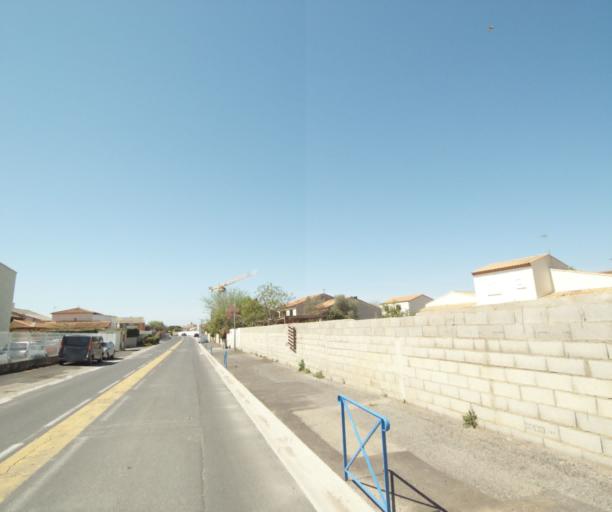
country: FR
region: Languedoc-Roussillon
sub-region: Departement de l'Herault
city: Saint-Bres
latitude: 43.6625
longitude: 4.0263
